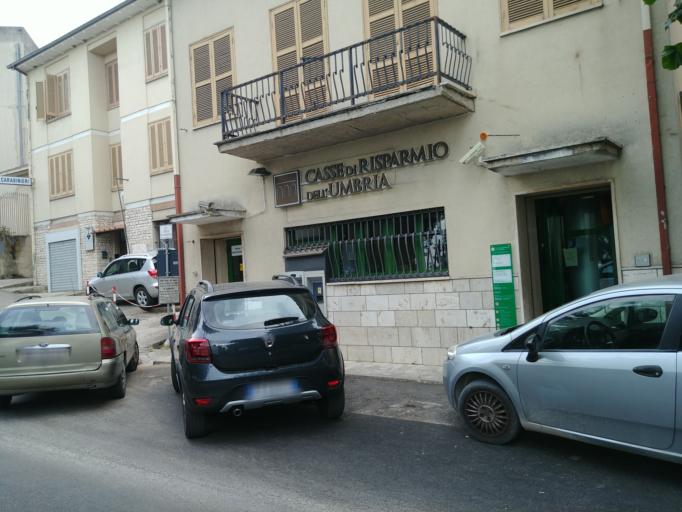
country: IT
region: Umbria
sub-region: Provincia di Terni
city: Stroncone
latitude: 42.4974
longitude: 12.6615
